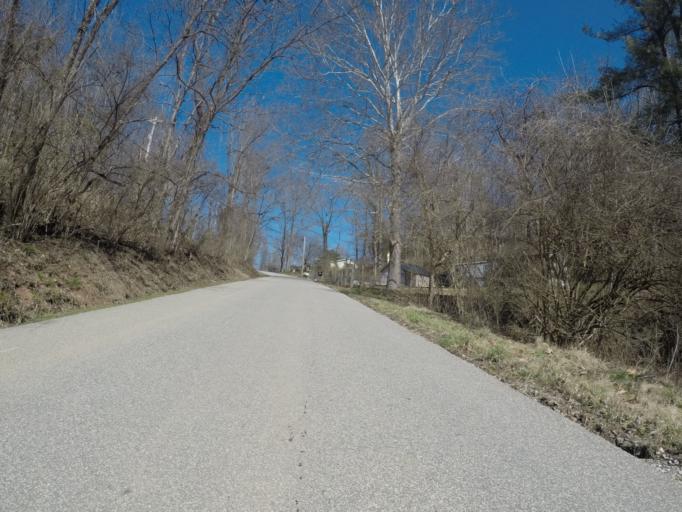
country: US
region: Ohio
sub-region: Lawrence County
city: Burlington
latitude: 38.4577
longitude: -82.5015
